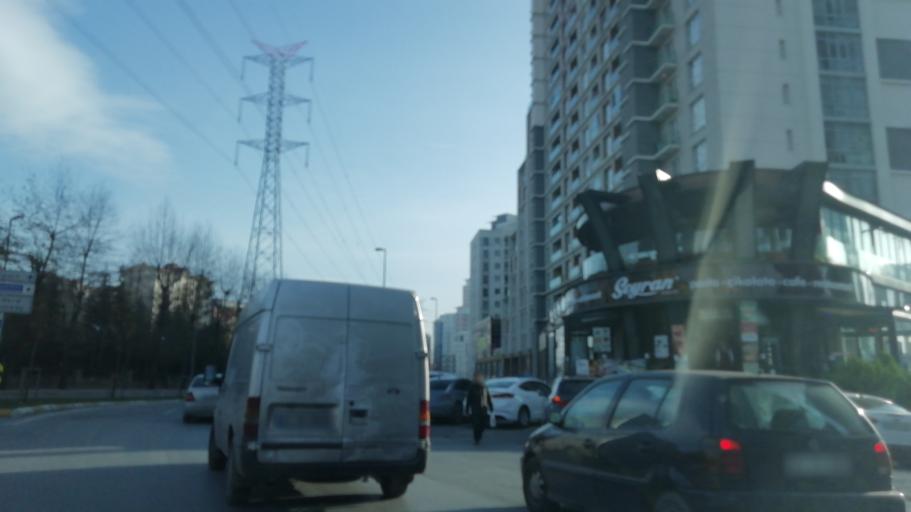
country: TR
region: Istanbul
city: Esenyurt
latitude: 41.0618
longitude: 28.6686
